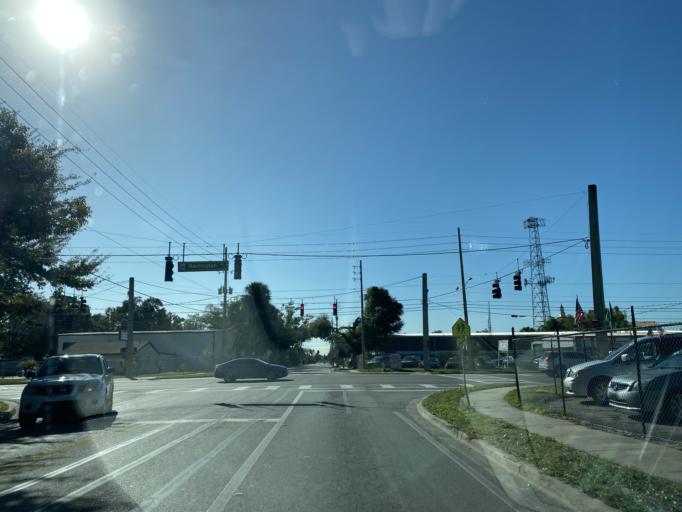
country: US
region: Florida
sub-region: Orange County
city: Orlando
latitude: 28.5447
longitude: -81.4056
